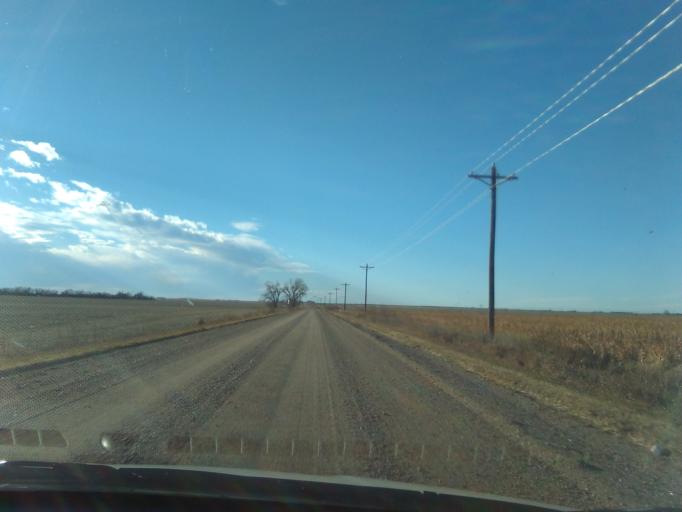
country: US
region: Nebraska
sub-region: Kearney County
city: Minden
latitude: 40.3650
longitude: -98.9955
